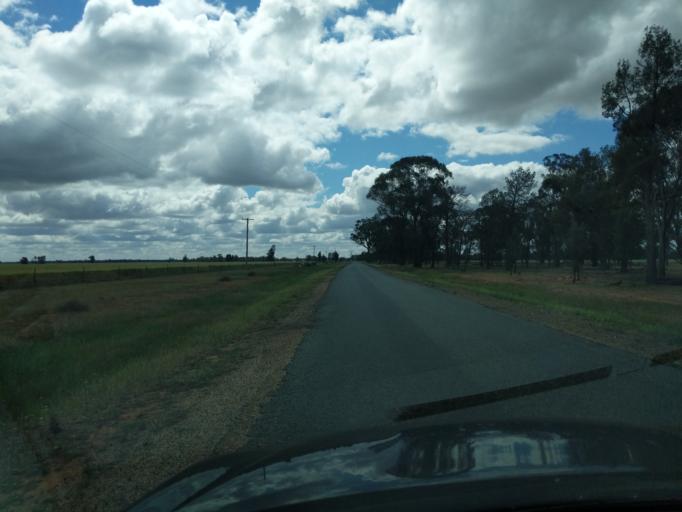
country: AU
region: New South Wales
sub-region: Coolamon
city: Coolamon
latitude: -34.8638
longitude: 146.8972
